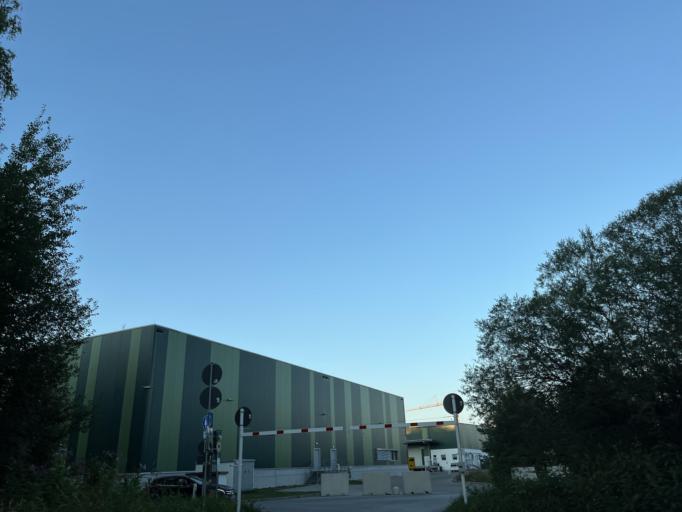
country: DE
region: Bavaria
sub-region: Upper Bavaria
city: Raubling
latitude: 47.7918
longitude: 12.0701
